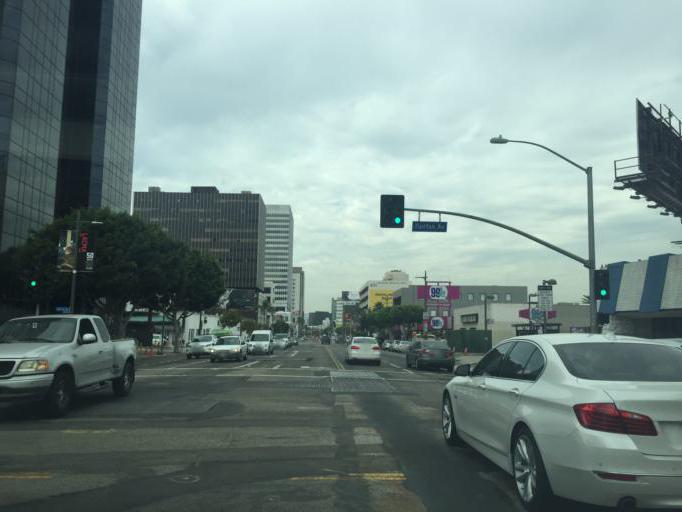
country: US
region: California
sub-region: Los Angeles County
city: West Hollywood
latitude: 34.0629
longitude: -118.3614
